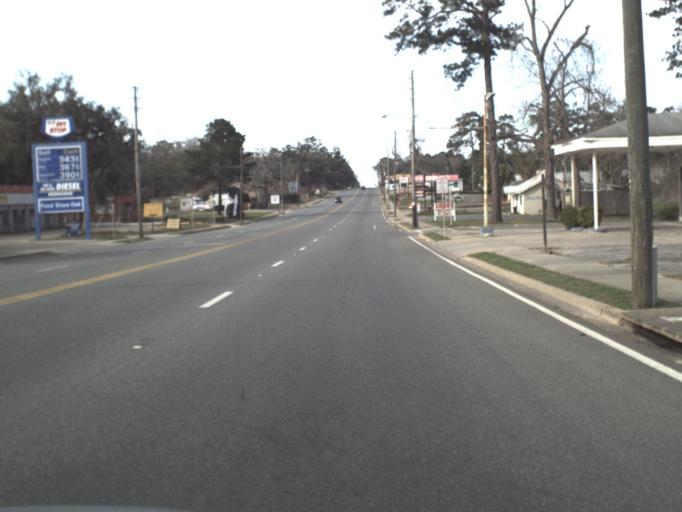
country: US
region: Florida
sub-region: Jefferson County
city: Monticello
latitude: 30.5518
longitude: -83.8701
